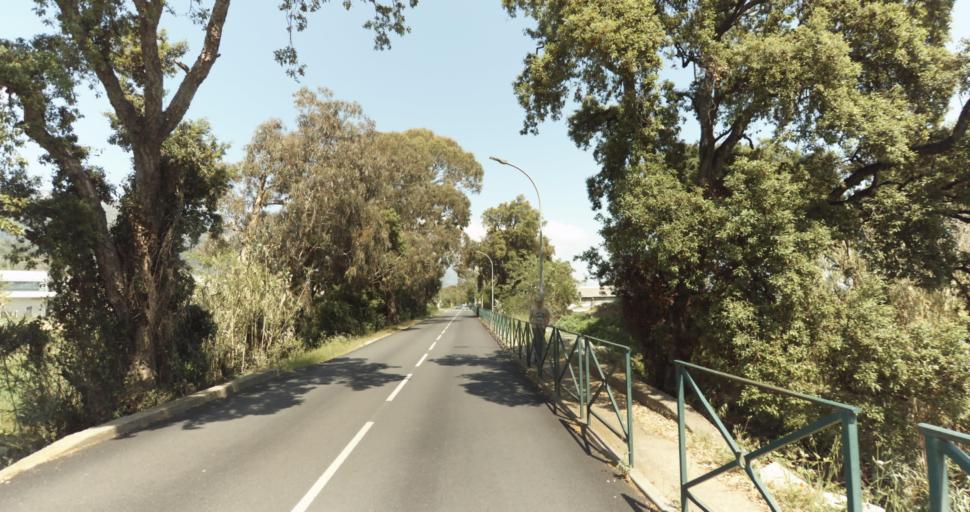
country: FR
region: Corsica
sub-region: Departement de la Haute-Corse
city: Biguglia
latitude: 42.6000
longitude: 9.4352
